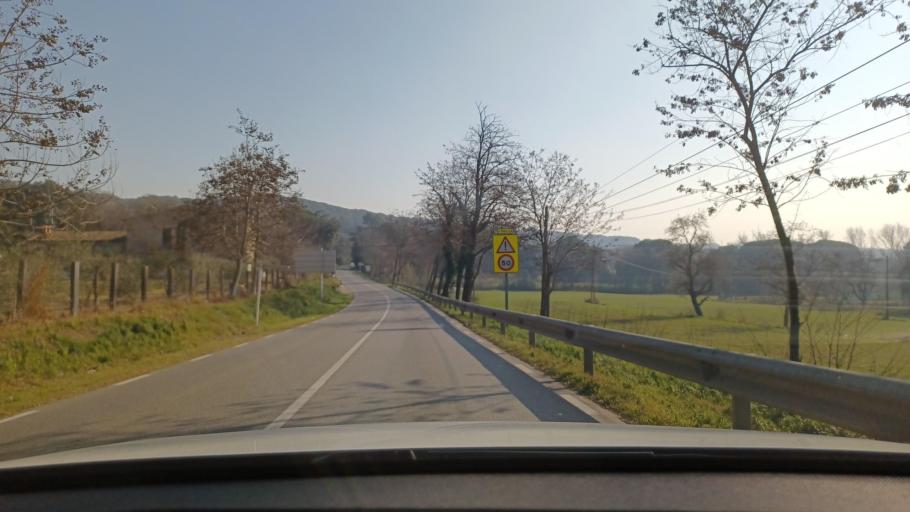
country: ES
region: Catalonia
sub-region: Provincia de Barcelona
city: Bigues i Riells
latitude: 41.6675
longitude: 2.2296
